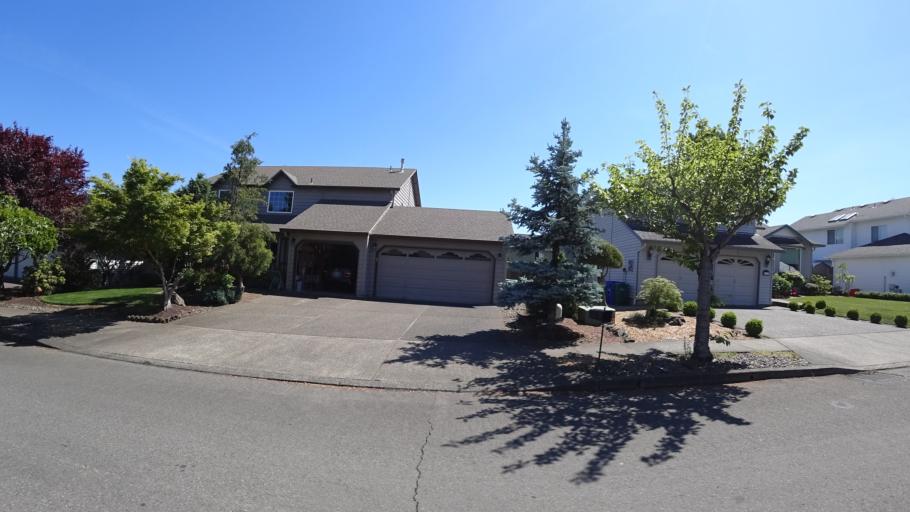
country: US
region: Oregon
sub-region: Multnomah County
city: Gresham
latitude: 45.4745
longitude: -122.4649
